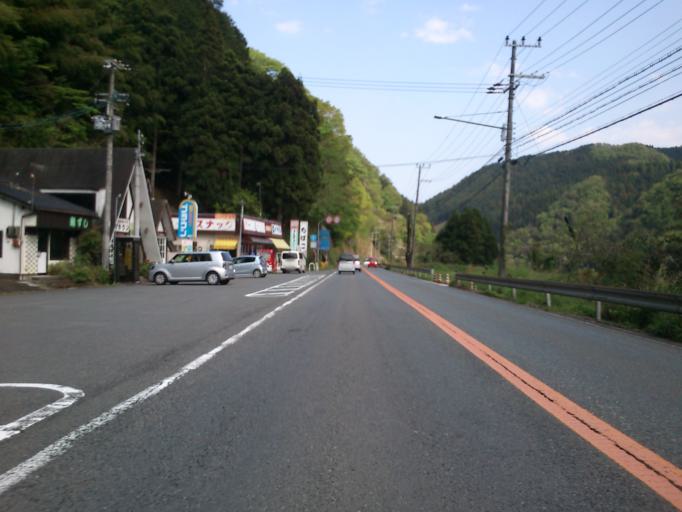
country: JP
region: Kyoto
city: Fukuchiyama
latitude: 35.3225
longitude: 134.9794
